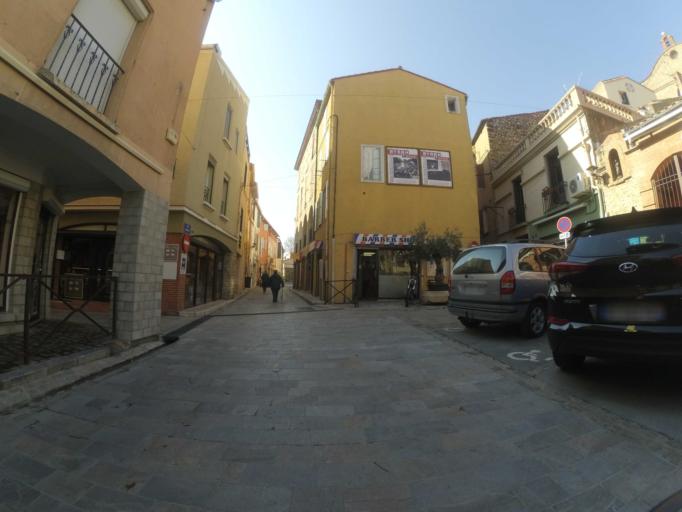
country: FR
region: Languedoc-Roussillon
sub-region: Departement des Pyrenees-Orientales
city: Thuir
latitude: 42.6333
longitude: 2.7558
